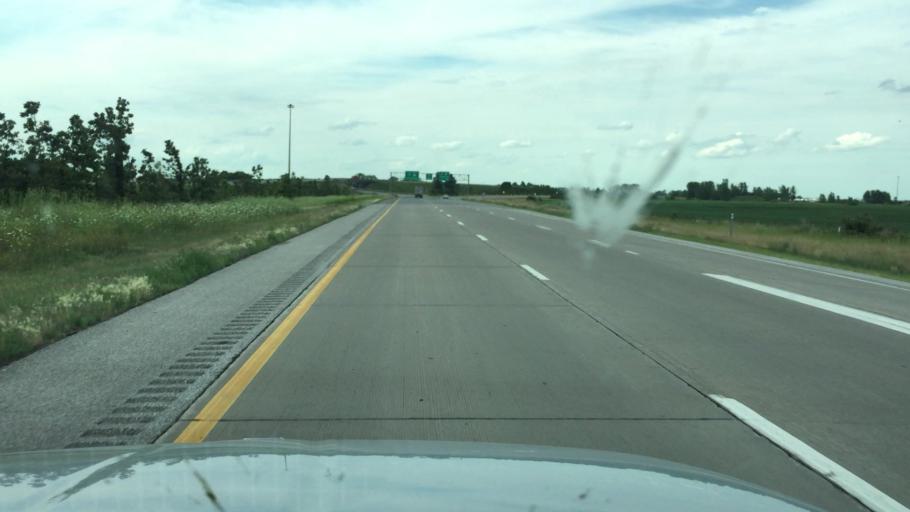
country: US
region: Iowa
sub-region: Scott County
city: Walcott
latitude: 41.5951
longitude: -90.6758
